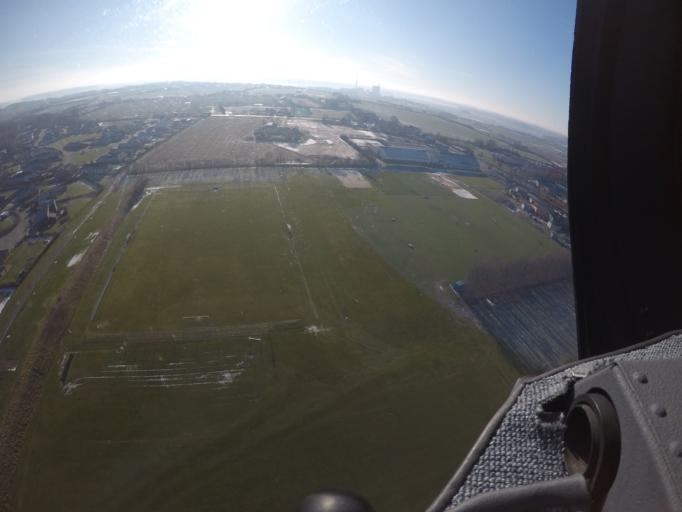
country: DK
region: South Denmark
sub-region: Fredericia Kommune
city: Taulov
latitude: 55.5362
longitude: 9.6243
